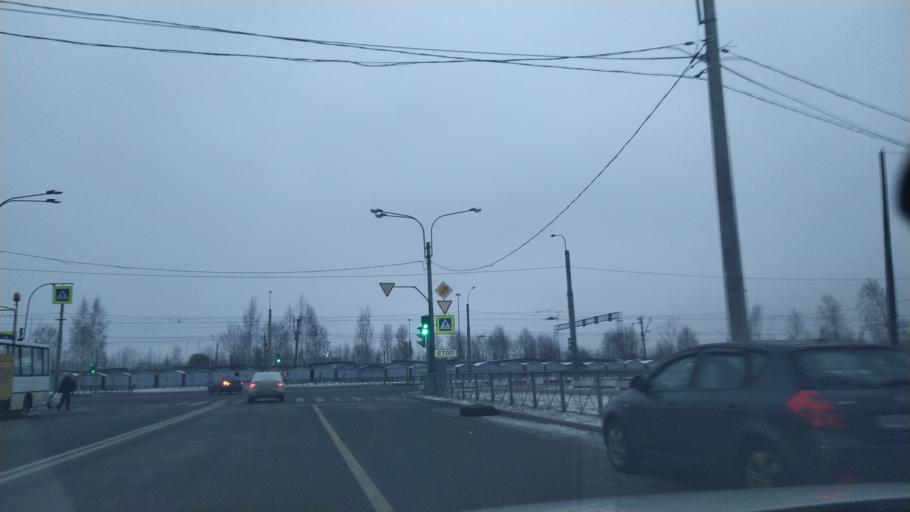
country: RU
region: St.-Petersburg
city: Grazhdanka
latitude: 60.0497
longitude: 30.3925
